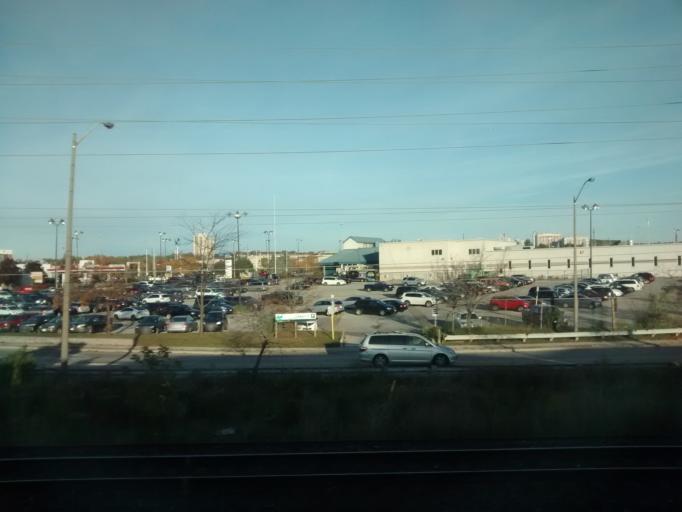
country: CA
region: Ontario
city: Oakville
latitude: 43.4576
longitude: -79.6797
